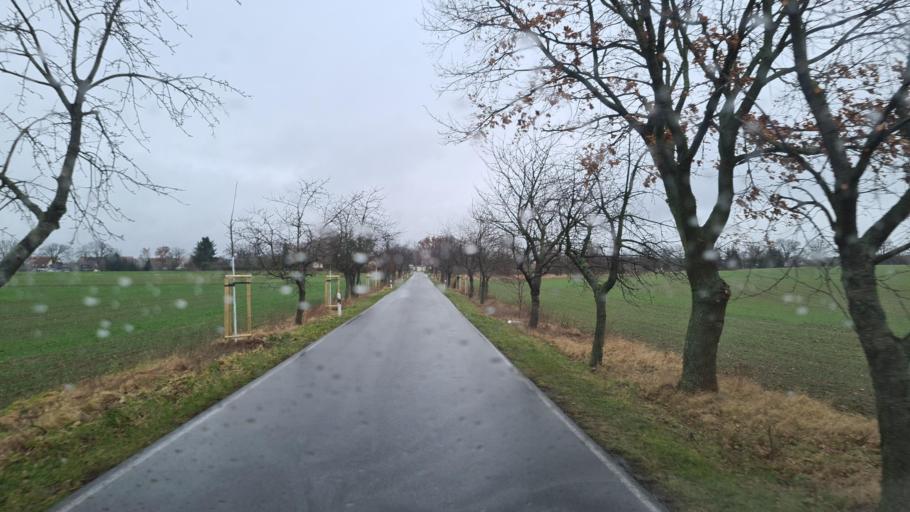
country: DE
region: Brandenburg
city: Gransee
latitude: 52.8943
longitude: 13.1999
